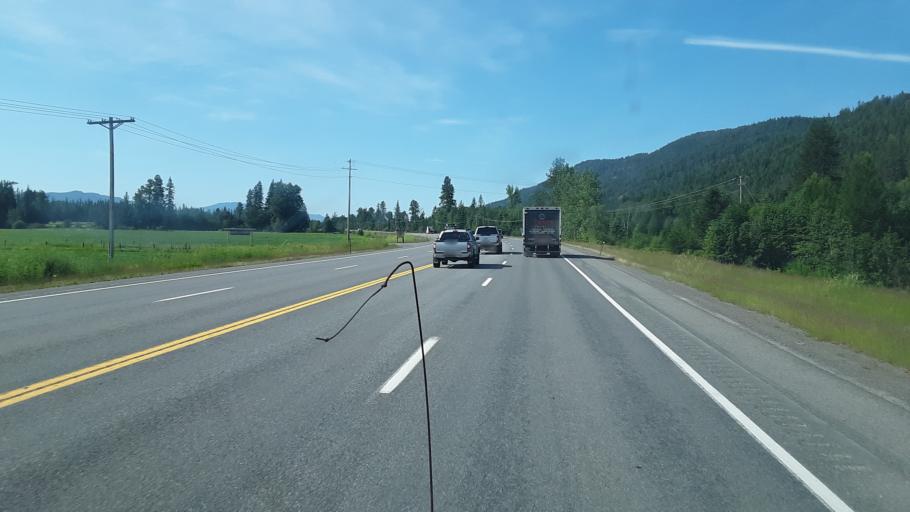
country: US
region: Idaho
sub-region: Bonner County
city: Ponderay
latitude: 48.3762
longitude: -116.5462
